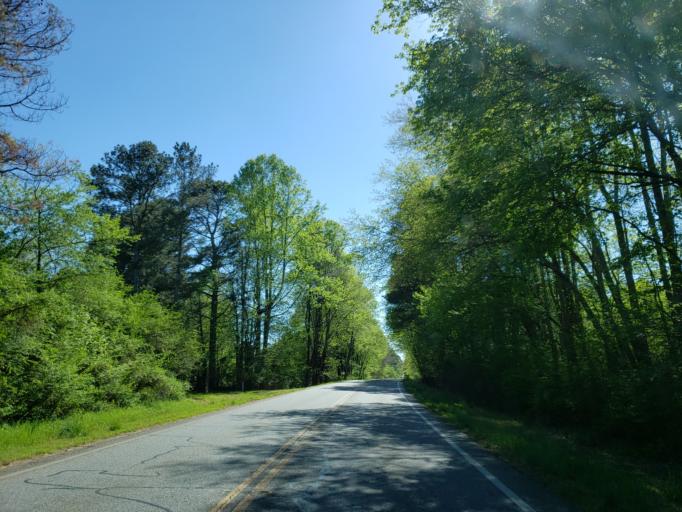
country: US
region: Georgia
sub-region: Cherokee County
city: Canton
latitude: 34.3421
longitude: -84.5159
